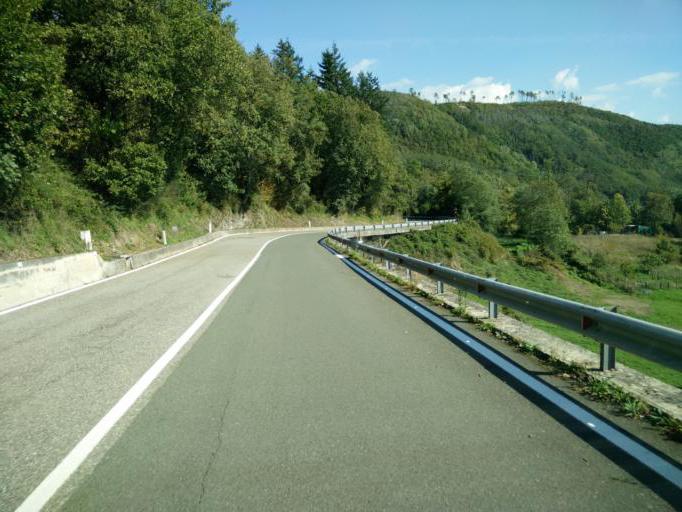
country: IT
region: Liguria
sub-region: Provincia di La Spezia
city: Carrodano
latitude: 44.2459
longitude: 9.6410
